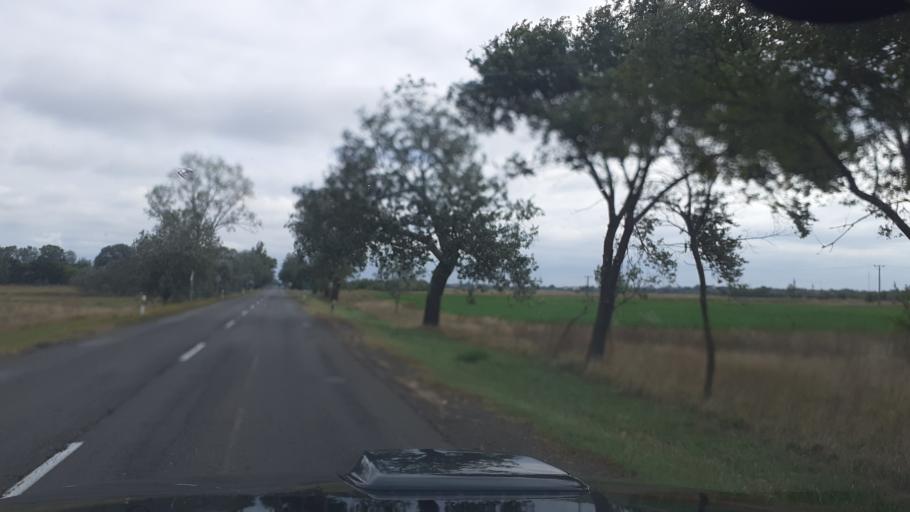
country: HU
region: Bacs-Kiskun
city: Fulopszallas
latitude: 46.8236
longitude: 19.2125
